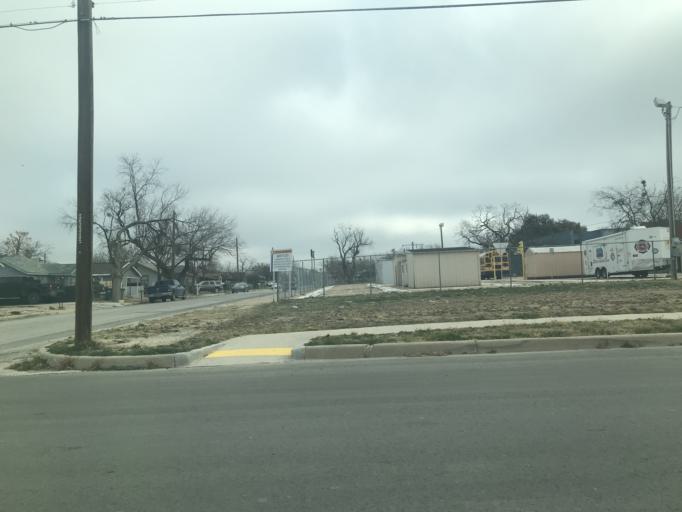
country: US
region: Texas
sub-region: Tom Green County
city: San Angelo
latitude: 31.4714
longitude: -100.4475
